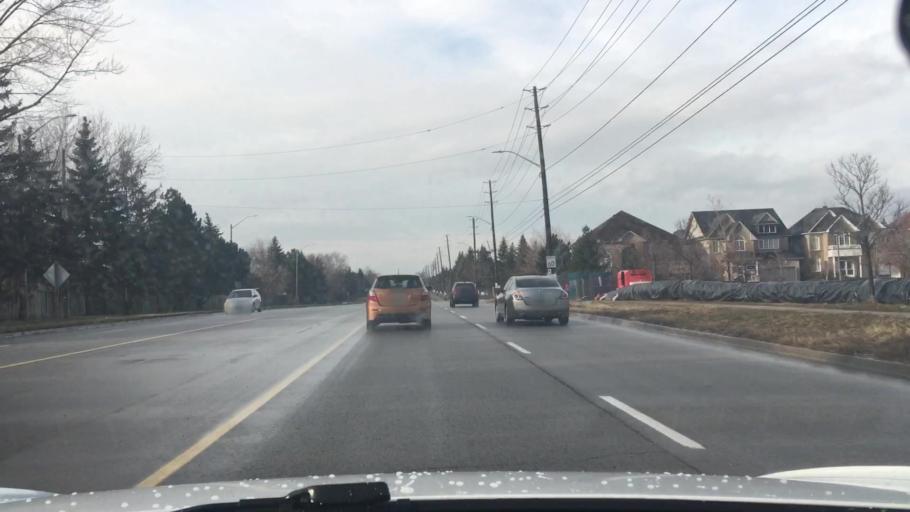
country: CA
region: Ontario
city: Markham
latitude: 43.8968
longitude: -79.2440
